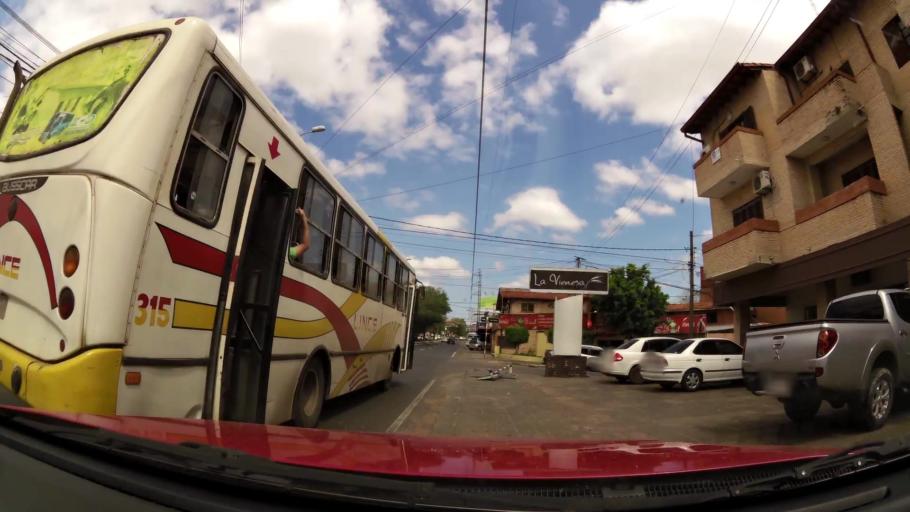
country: PY
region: Central
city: Fernando de la Mora
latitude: -25.3169
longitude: -57.5264
